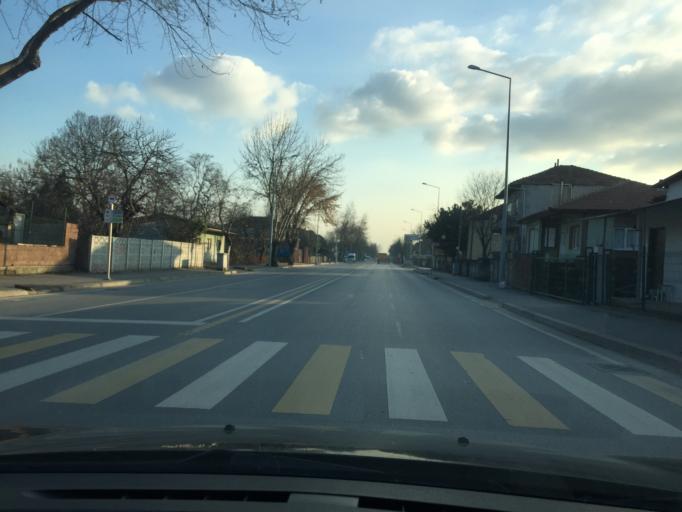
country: TR
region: Sakarya
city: Adapazari
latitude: 40.7993
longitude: 30.4065
